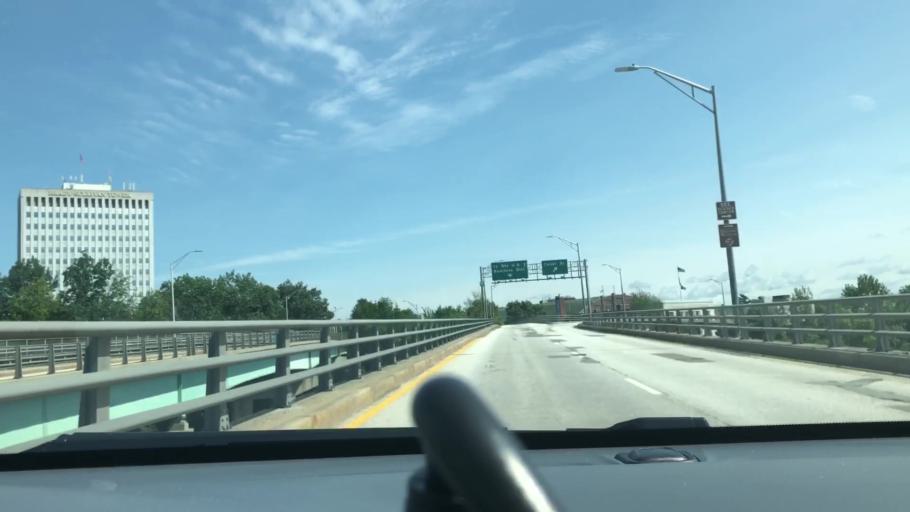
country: US
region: New Hampshire
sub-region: Hillsborough County
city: Manchester
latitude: 43.0037
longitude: -71.4699
